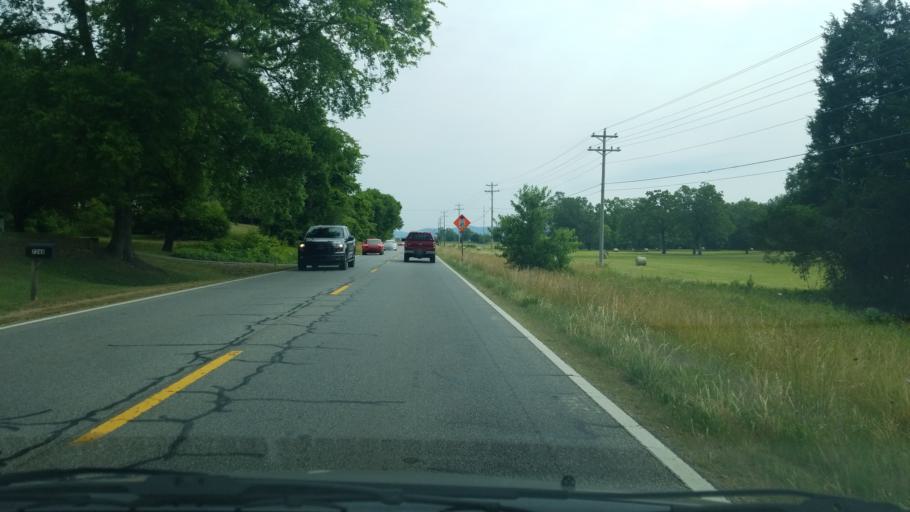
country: US
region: Georgia
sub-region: Catoosa County
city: Ringgold
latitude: 34.8880
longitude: -85.1349
